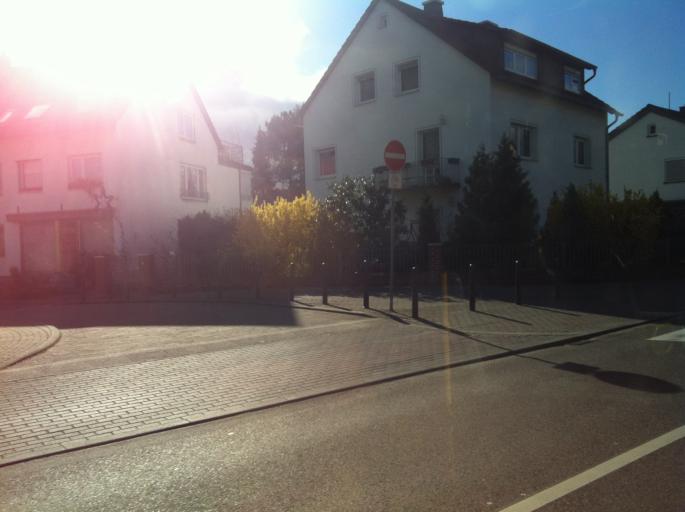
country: DE
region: Hesse
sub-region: Regierungsbezirk Darmstadt
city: Hochheim am Main
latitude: 50.0176
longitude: 8.3558
